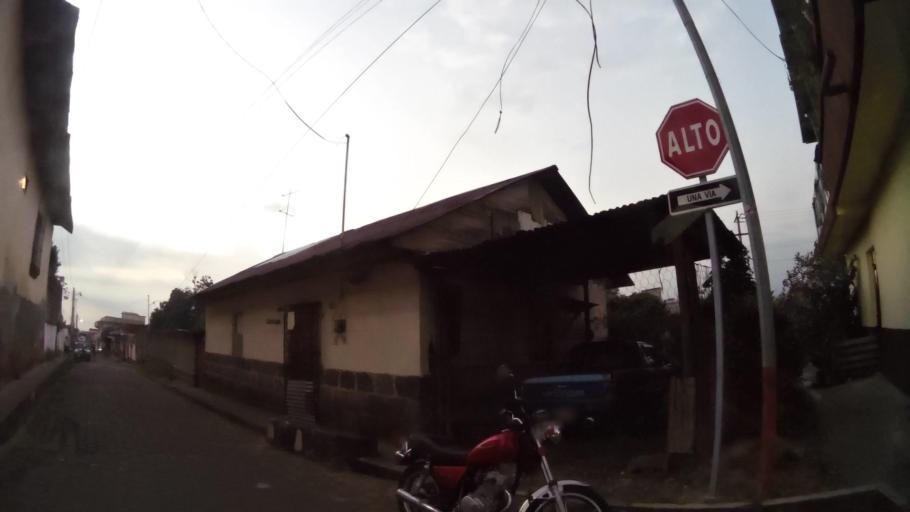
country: GT
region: Retalhuleu
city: San Felipe
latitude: 14.6257
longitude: -91.5952
